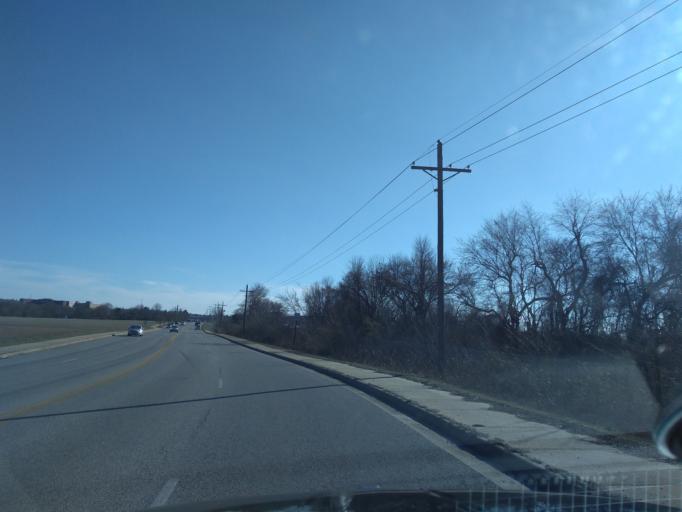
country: US
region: Arkansas
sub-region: Washington County
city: Johnson
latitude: 36.1216
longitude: -94.1632
